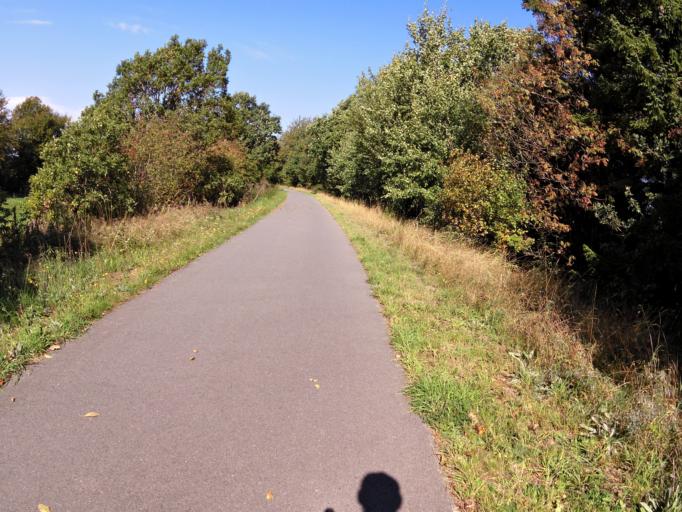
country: BE
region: Wallonia
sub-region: Province de Liege
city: Waimes
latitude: 50.4490
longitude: 6.1543
